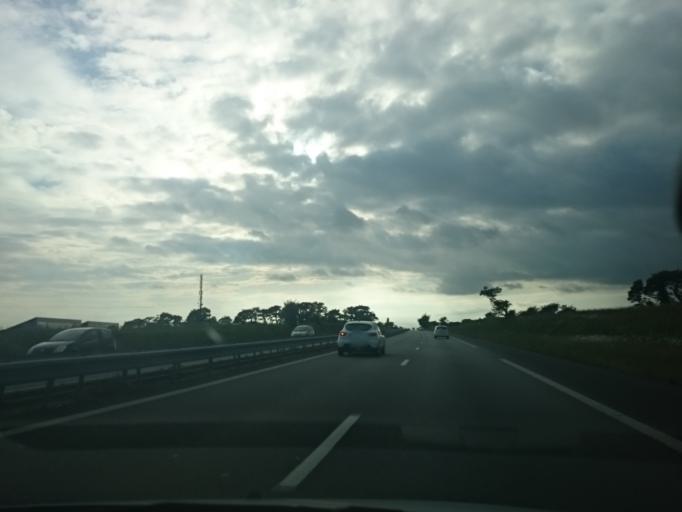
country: FR
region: Brittany
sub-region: Departement du Morbihan
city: Surzur
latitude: 47.5997
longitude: -2.5831
